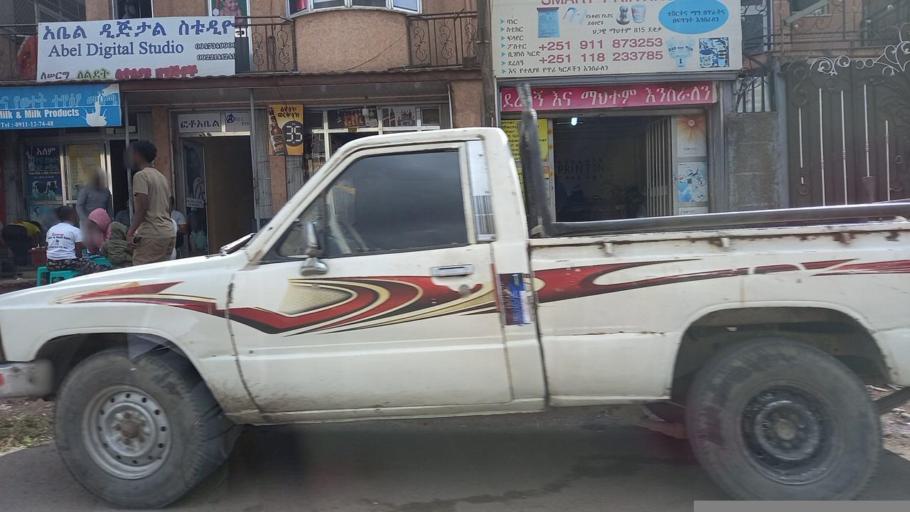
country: ET
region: Adis Abeba
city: Addis Ababa
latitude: 9.0098
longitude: 38.8539
